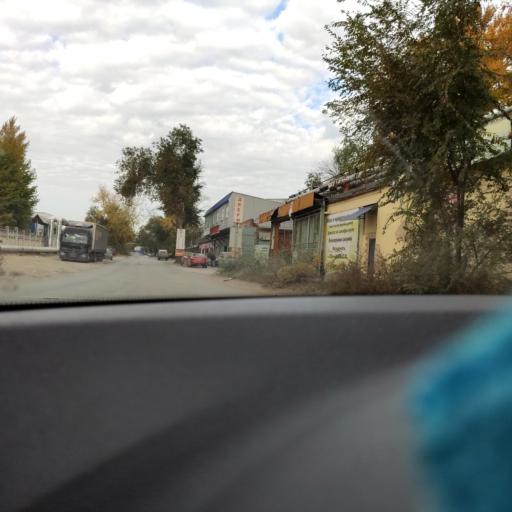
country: RU
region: Samara
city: Samara
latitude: 53.1958
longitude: 50.2604
